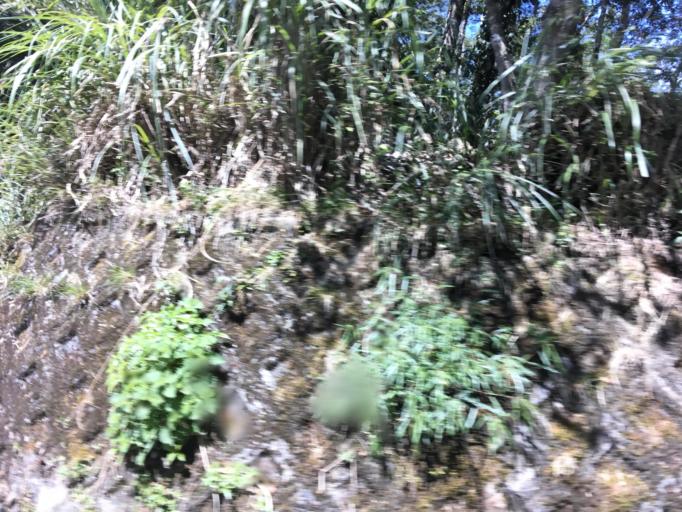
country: TW
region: Taiwan
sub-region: Yilan
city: Yilan
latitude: 24.5110
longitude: 121.5247
